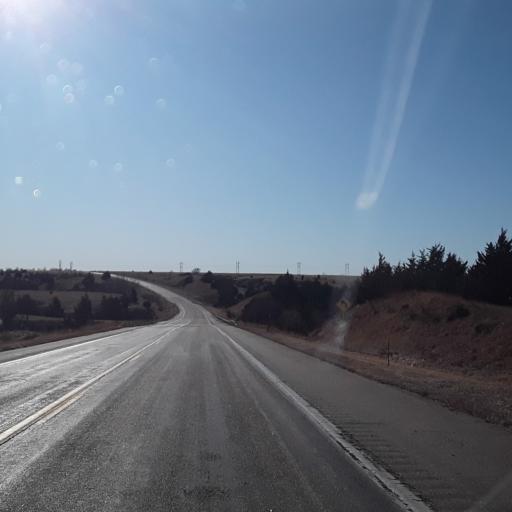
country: US
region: Nebraska
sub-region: Frontier County
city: Stockville
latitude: 40.5456
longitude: -100.6437
